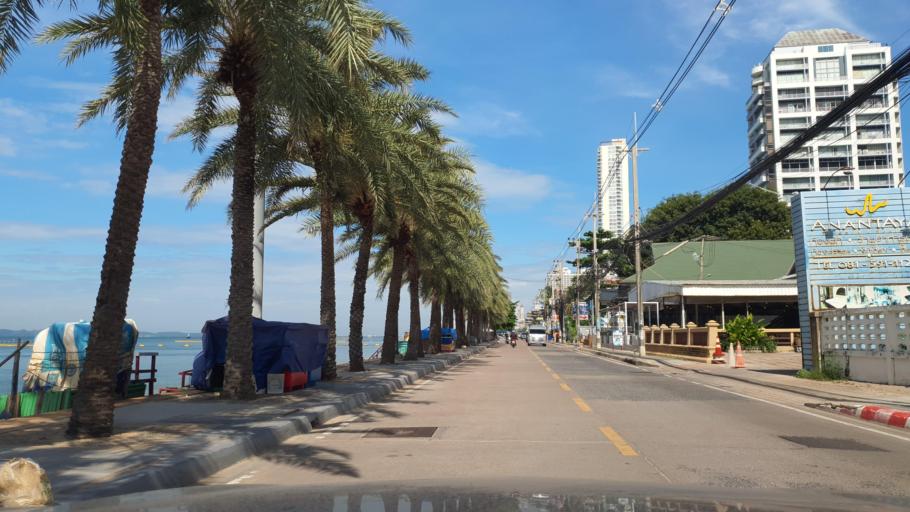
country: TH
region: Chon Buri
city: Phatthaya
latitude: 12.8699
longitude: 100.8902
